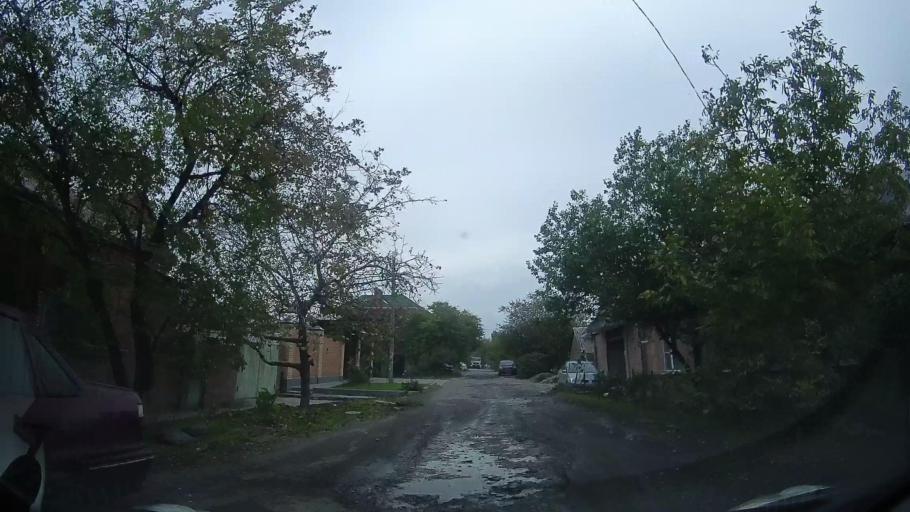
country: RU
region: Rostov
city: Severnyy
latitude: 47.2671
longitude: 39.6780
